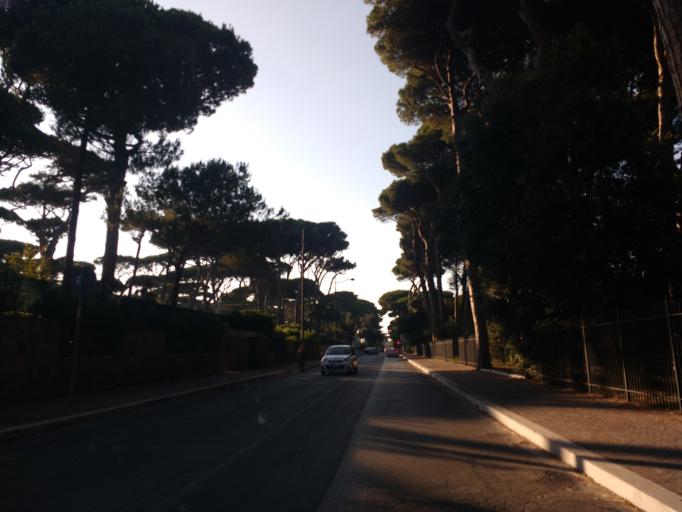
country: IT
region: Latium
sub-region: Citta metropolitana di Roma Capitale
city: Fregene
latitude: 41.8543
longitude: 12.1992
